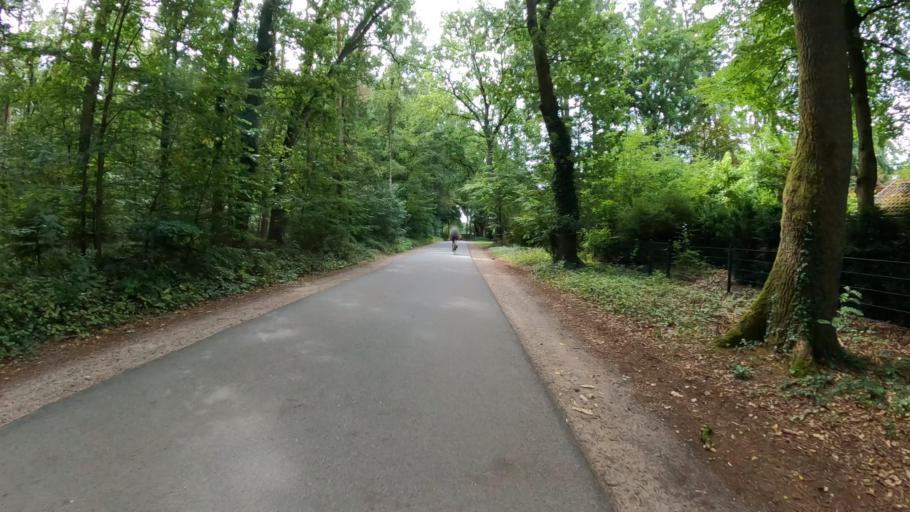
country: DE
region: Lower Saxony
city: Wenzendorf
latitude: 53.3616
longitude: 9.7558
